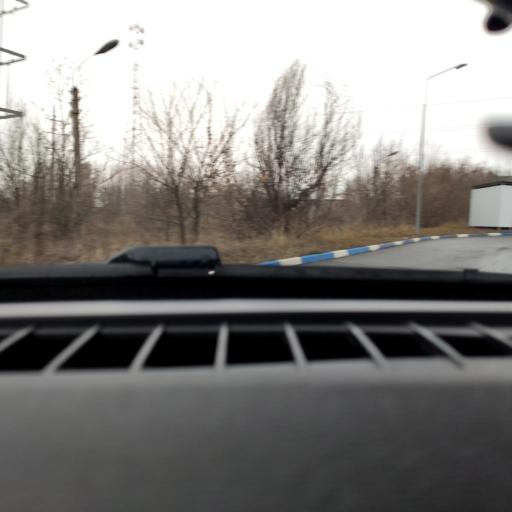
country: RU
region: Voronezj
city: Semiluki
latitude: 51.6864
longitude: 38.9866
